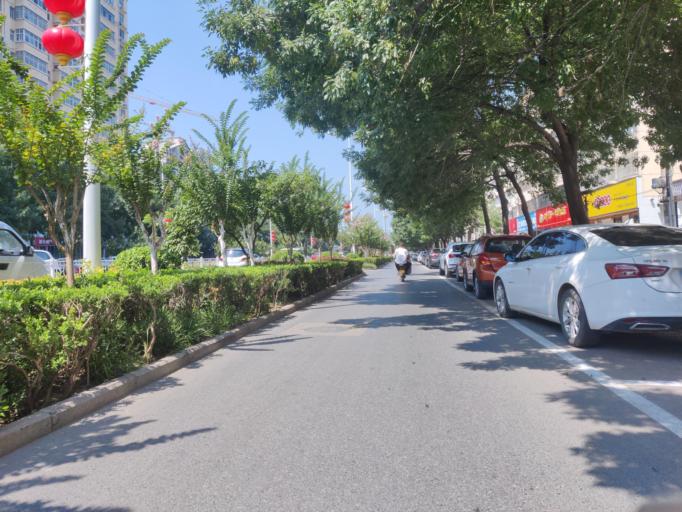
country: CN
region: Henan Sheng
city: Puyang
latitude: 35.7725
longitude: 115.0247
